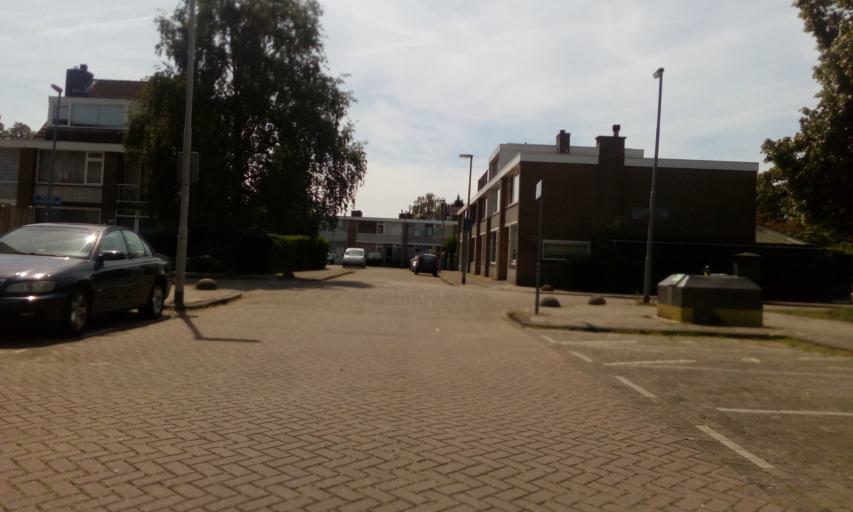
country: NL
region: South Holland
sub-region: Gemeente Rotterdam
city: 's-Gravenland
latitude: 51.9446
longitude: 4.5351
